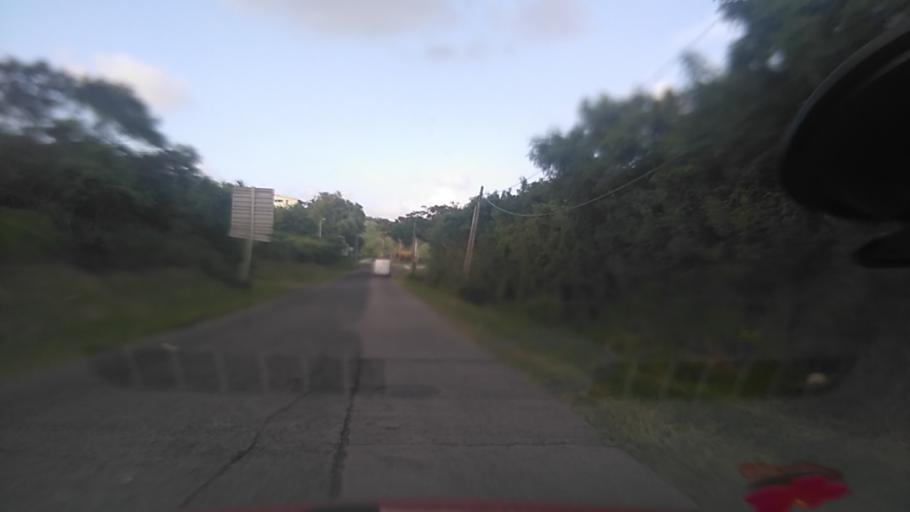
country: MQ
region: Martinique
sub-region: Martinique
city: Le Marin
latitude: 14.4691
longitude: -60.8583
